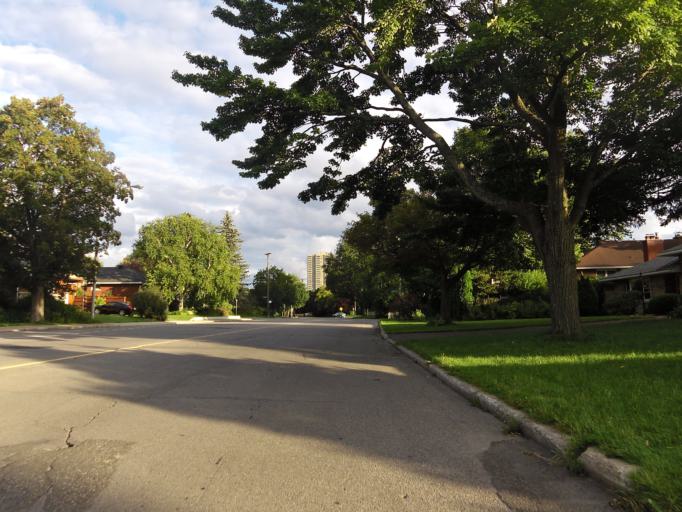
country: CA
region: Ontario
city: Ottawa
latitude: 45.3792
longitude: -75.7681
